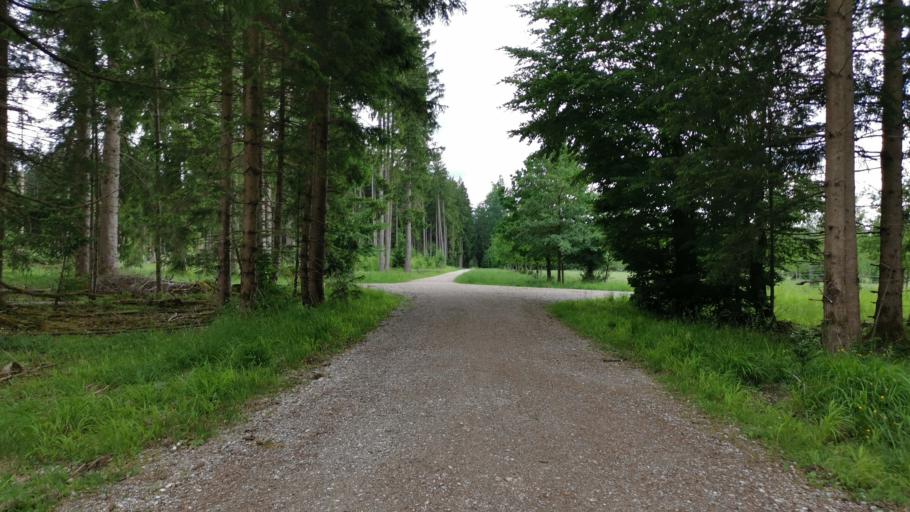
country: DE
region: Bavaria
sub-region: Upper Bavaria
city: Baierbrunn
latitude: 48.0477
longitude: 11.4897
